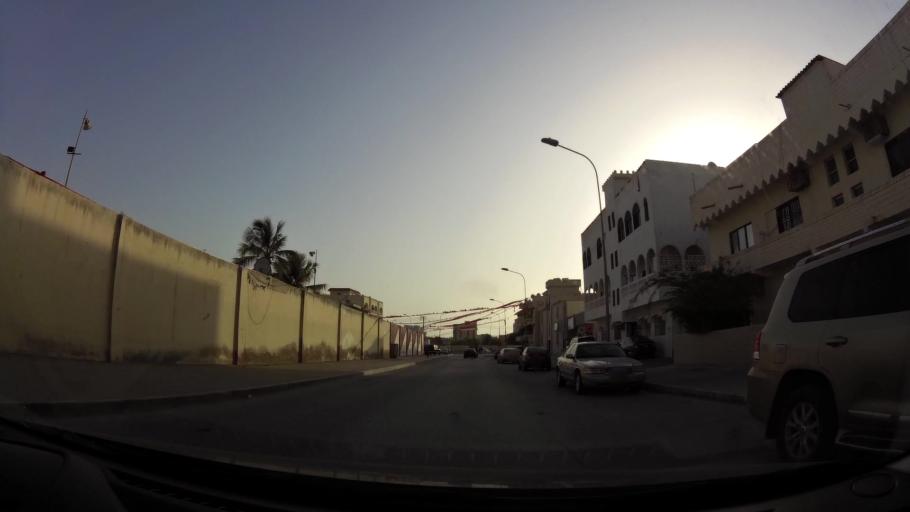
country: OM
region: Zufar
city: Salalah
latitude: 17.0147
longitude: 54.0978
